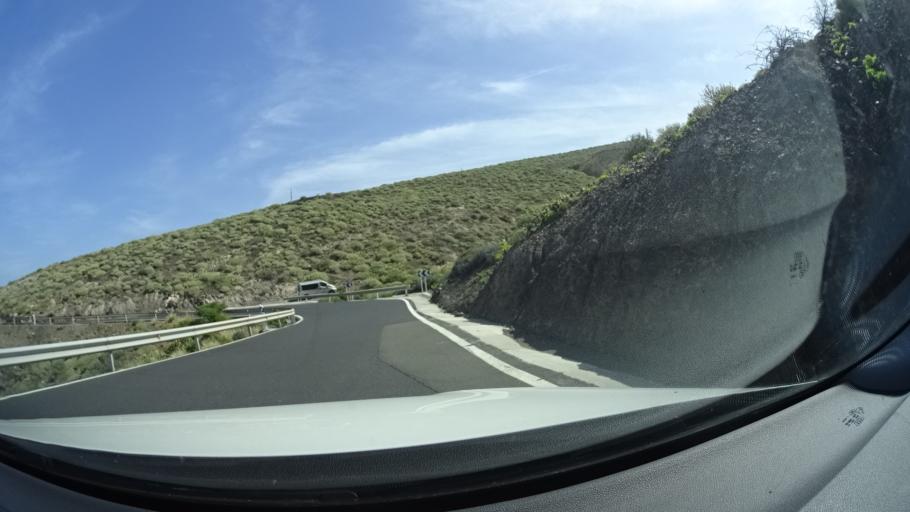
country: ES
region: Canary Islands
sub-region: Provincia de Las Palmas
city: Agaete
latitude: 28.0918
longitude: -15.7065
